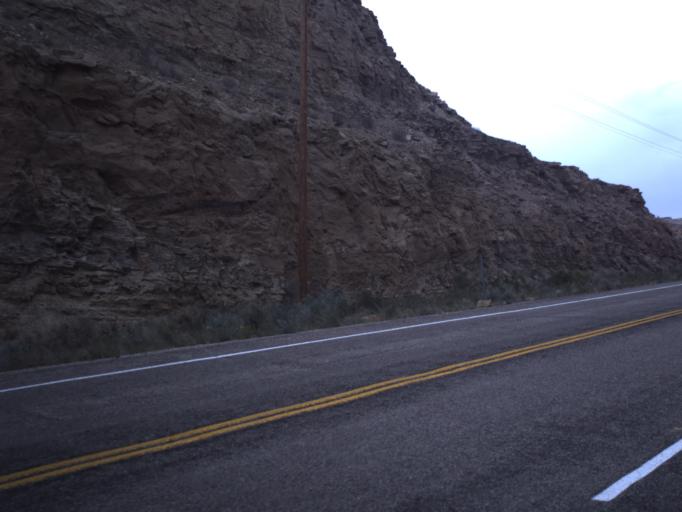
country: US
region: Colorado
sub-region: Rio Blanco County
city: Rangely
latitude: 39.9862
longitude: -109.1778
